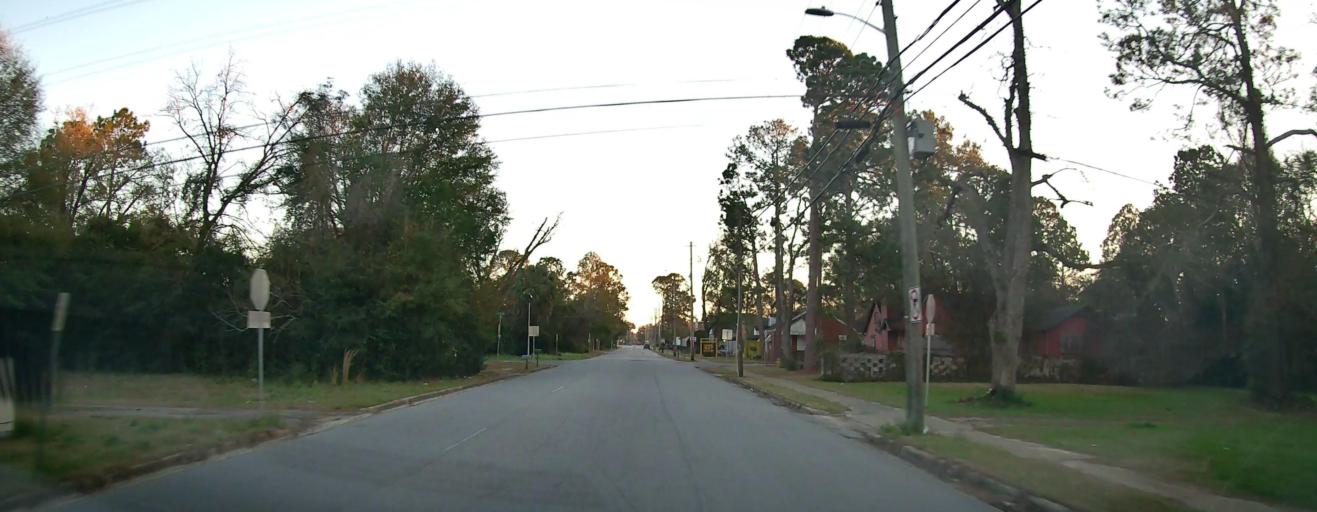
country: US
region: Georgia
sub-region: Dougherty County
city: Albany
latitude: 31.5670
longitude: -84.1619
